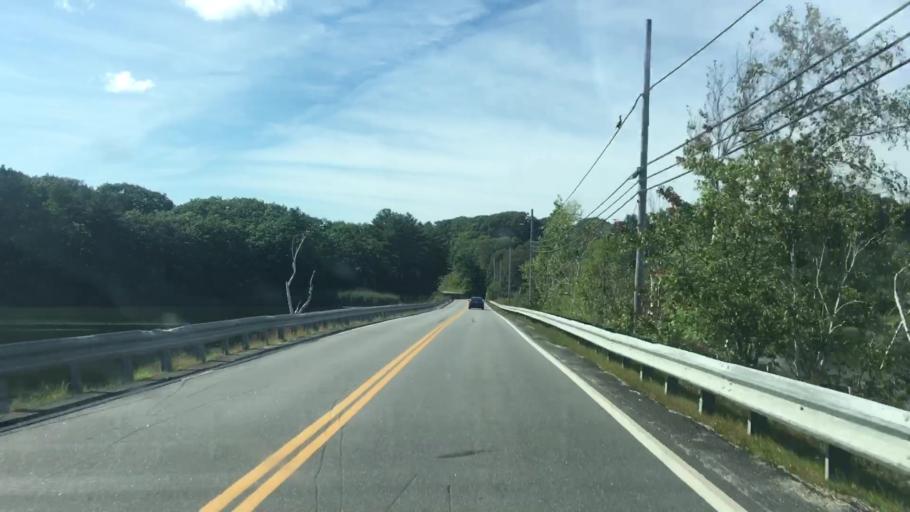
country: US
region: Maine
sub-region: Sagadahoc County
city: North Bath
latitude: 43.9318
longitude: -69.8630
